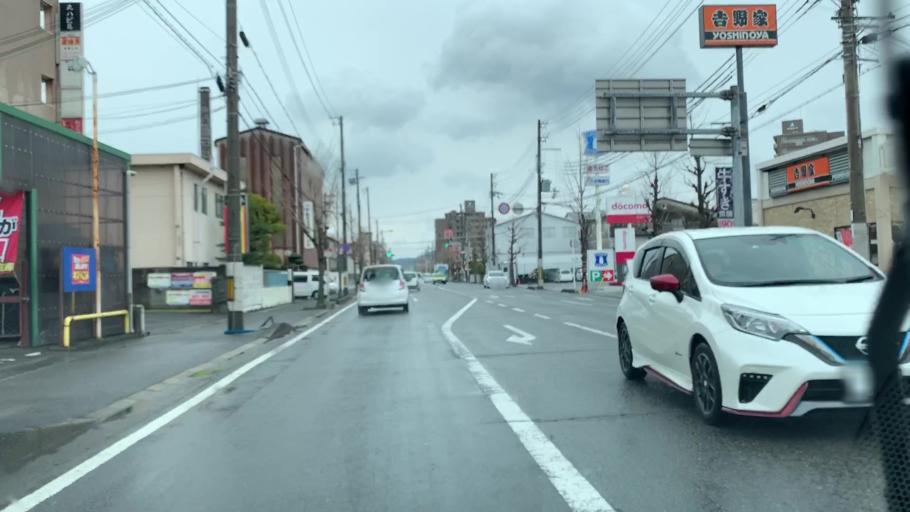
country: JP
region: Wakayama
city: Wakayama-shi
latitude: 34.2242
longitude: 135.1596
